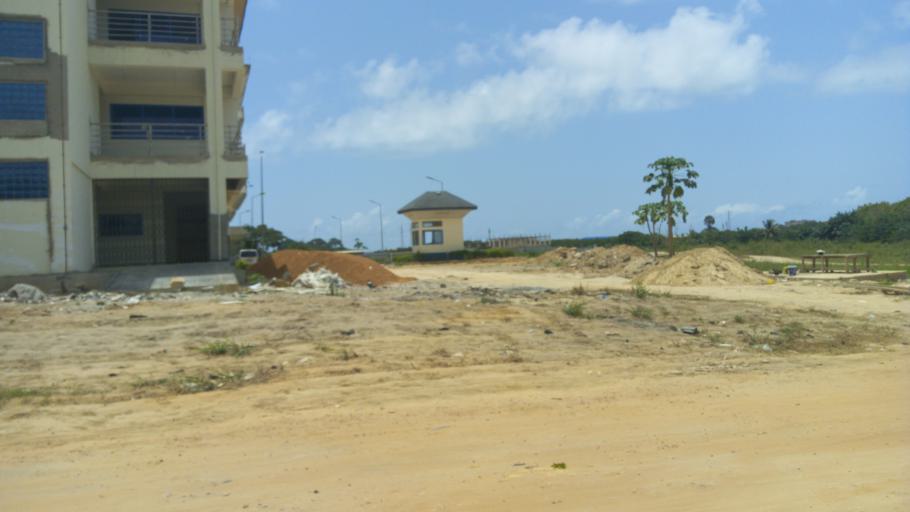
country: GH
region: Central
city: Cape Coast
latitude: 5.1228
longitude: -1.2951
